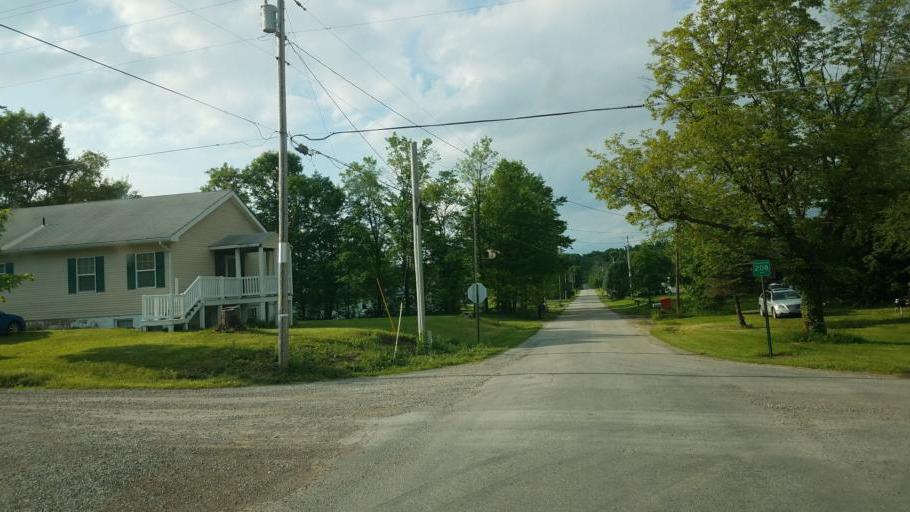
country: US
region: Ohio
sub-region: Knox County
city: Centerburg
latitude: 40.3910
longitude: -82.7606
